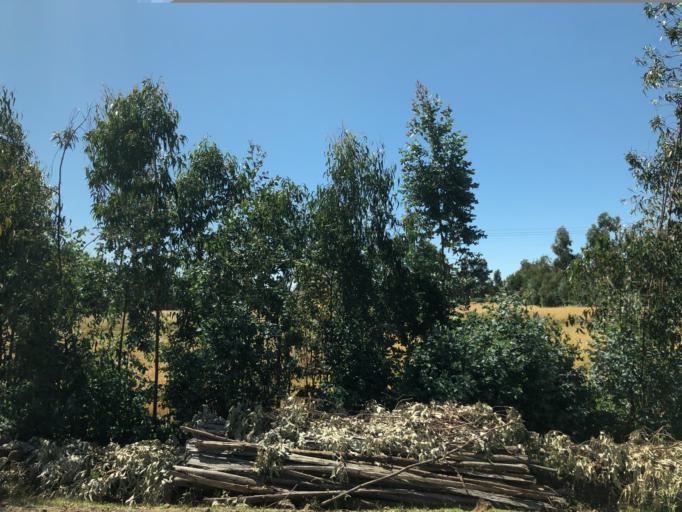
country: ET
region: Amhara
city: Lalibela
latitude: 11.7278
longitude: 38.7609
